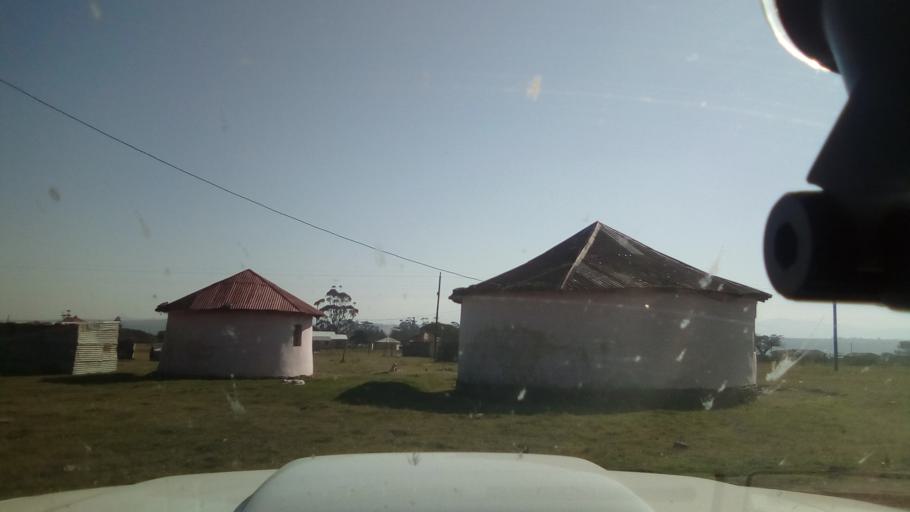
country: ZA
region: Eastern Cape
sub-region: Buffalo City Metropolitan Municipality
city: Bhisho
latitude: -32.9429
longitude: 27.3367
